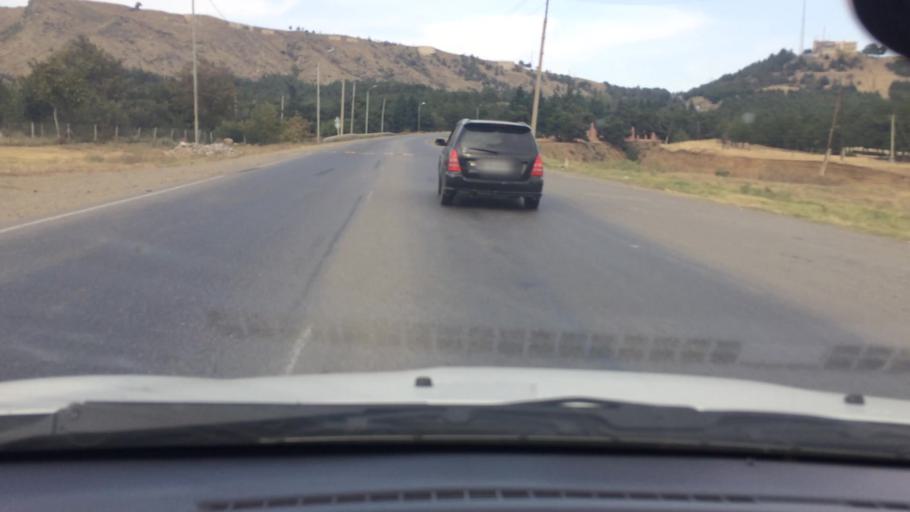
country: GE
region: T'bilisi
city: Tbilisi
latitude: 41.6188
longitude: 44.7941
